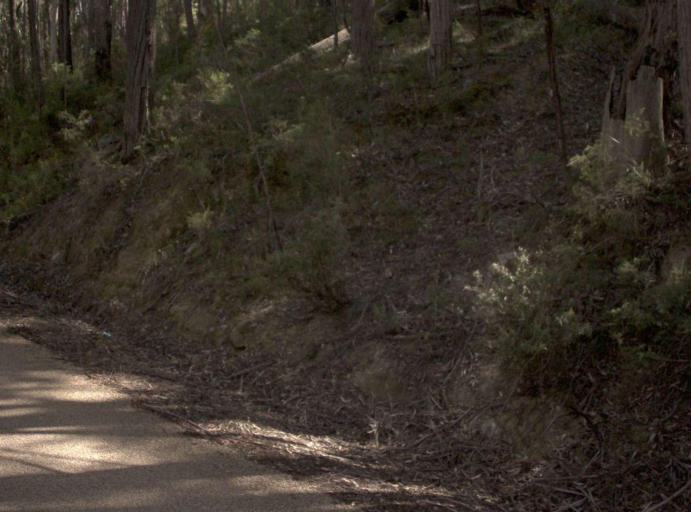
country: AU
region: Victoria
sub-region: East Gippsland
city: Lakes Entrance
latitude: -37.4095
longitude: 148.1227
